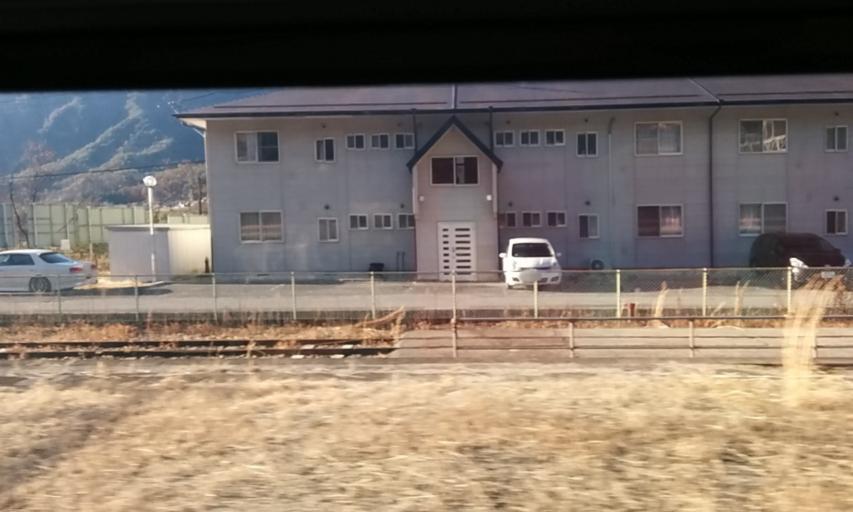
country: JP
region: Nagano
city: Iida
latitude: 35.6984
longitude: 137.6953
